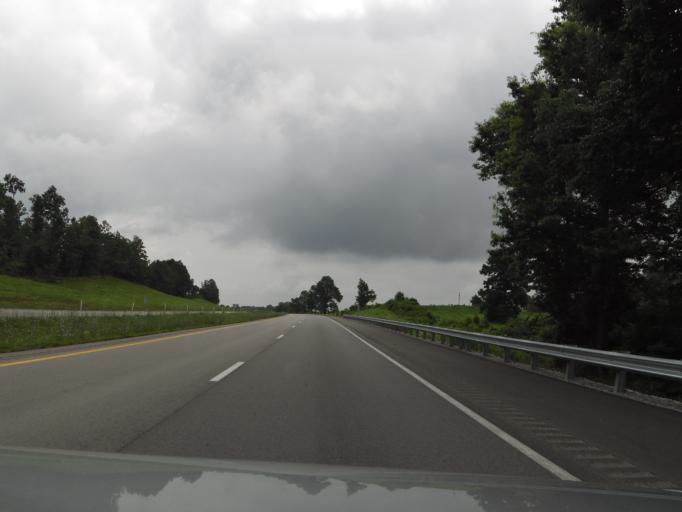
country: US
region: Kentucky
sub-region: Grayson County
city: Leitchfield
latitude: 37.4433
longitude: -86.3582
